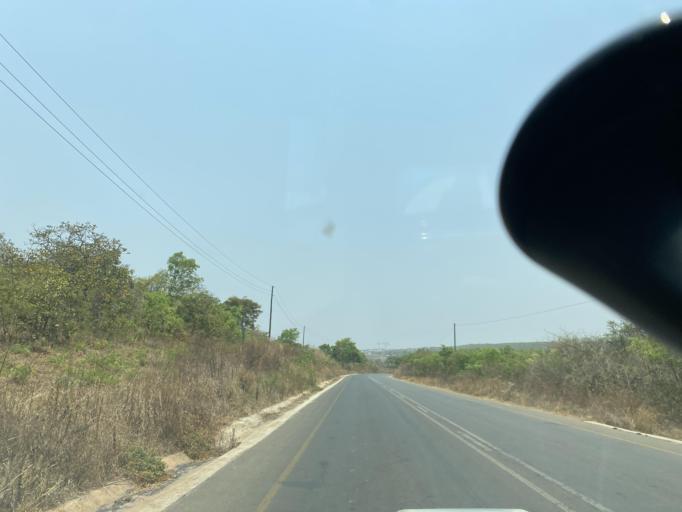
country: ZM
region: Lusaka
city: Lusaka
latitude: -15.5427
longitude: 28.4745
